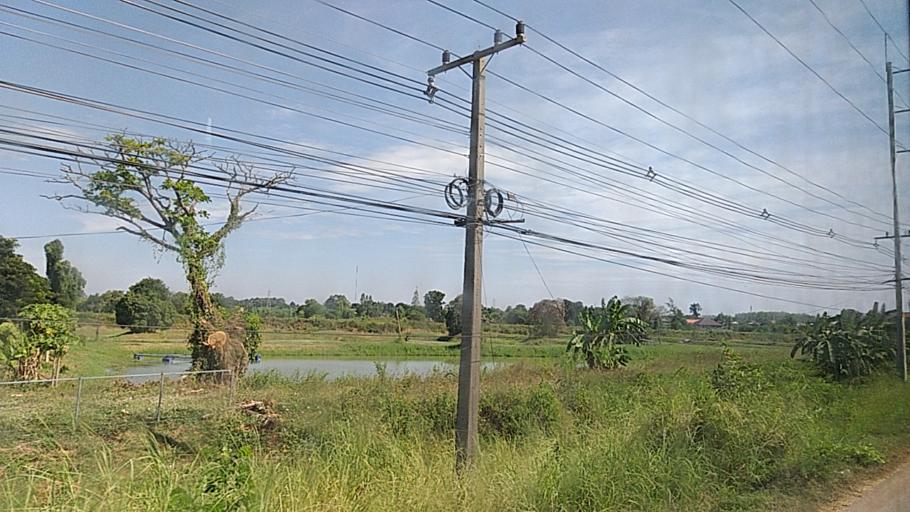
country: TH
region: Khon Kaen
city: Khon Kaen
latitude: 16.4379
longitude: 102.9372
